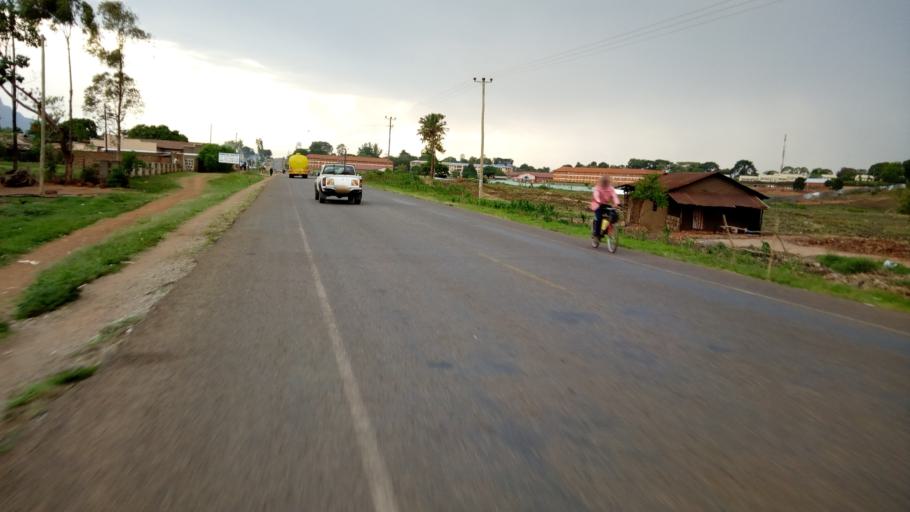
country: UG
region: Eastern Region
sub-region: Mbale District
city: Mbale
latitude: 1.1070
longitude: 34.1730
